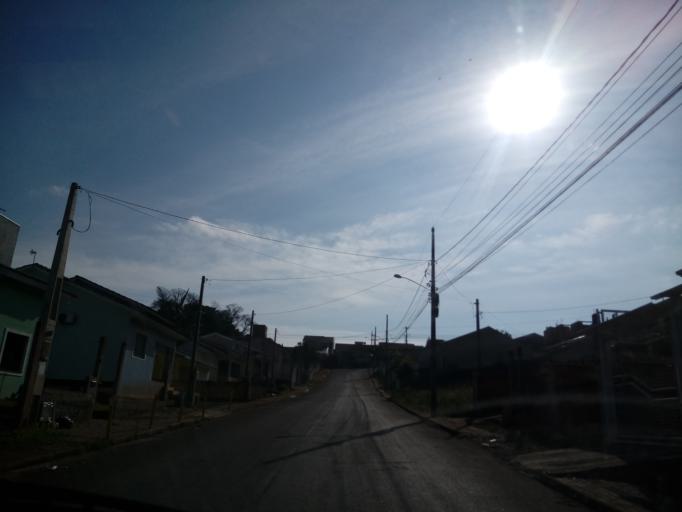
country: BR
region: Santa Catarina
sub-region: Chapeco
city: Chapeco
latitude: -27.1060
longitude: -52.5889
